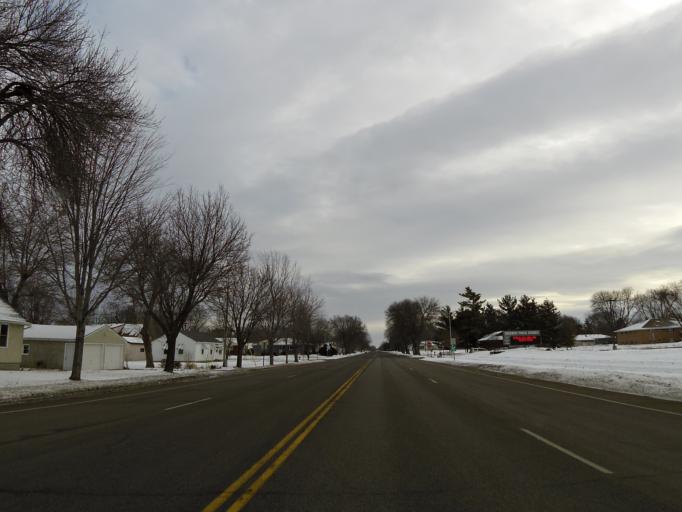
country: US
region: Minnesota
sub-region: Scott County
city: Shakopee
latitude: 44.7883
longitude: -93.5216
